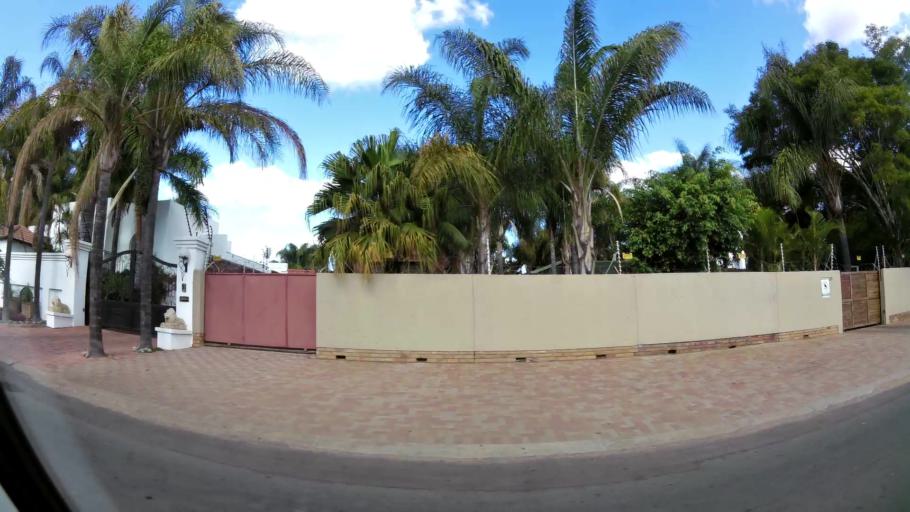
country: ZA
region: Limpopo
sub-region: Capricorn District Municipality
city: Polokwane
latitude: -23.8956
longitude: 29.4754
